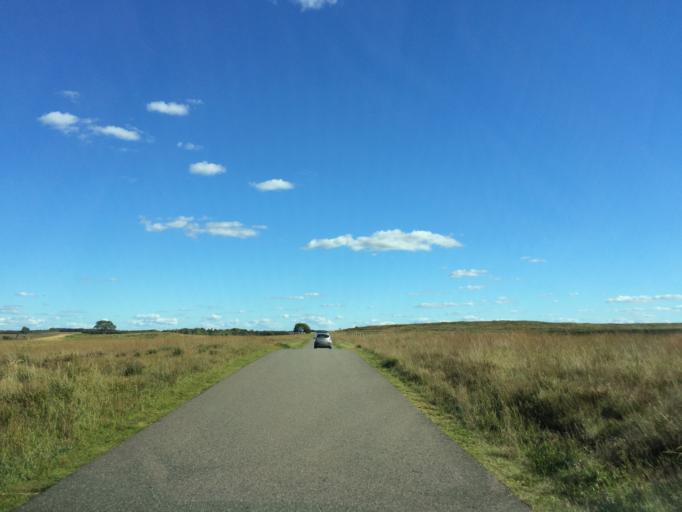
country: DK
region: Central Jutland
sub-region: Holstebro Kommune
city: Holstebro
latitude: 56.2703
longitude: 8.5150
